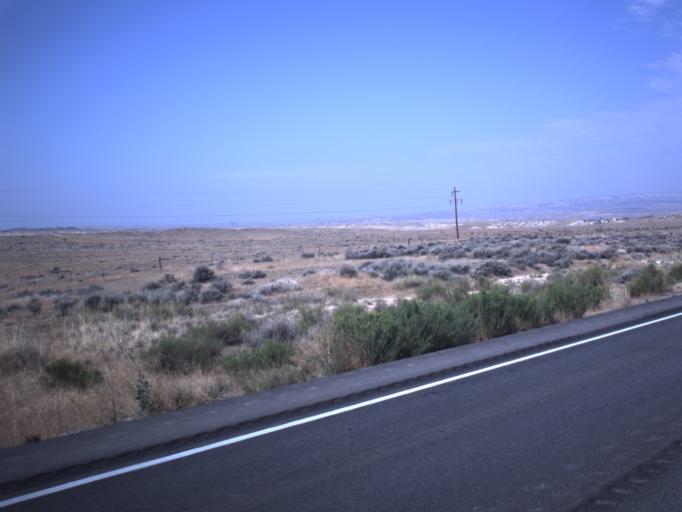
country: US
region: Utah
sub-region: Uintah County
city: Naples
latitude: 40.3296
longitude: -109.2770
